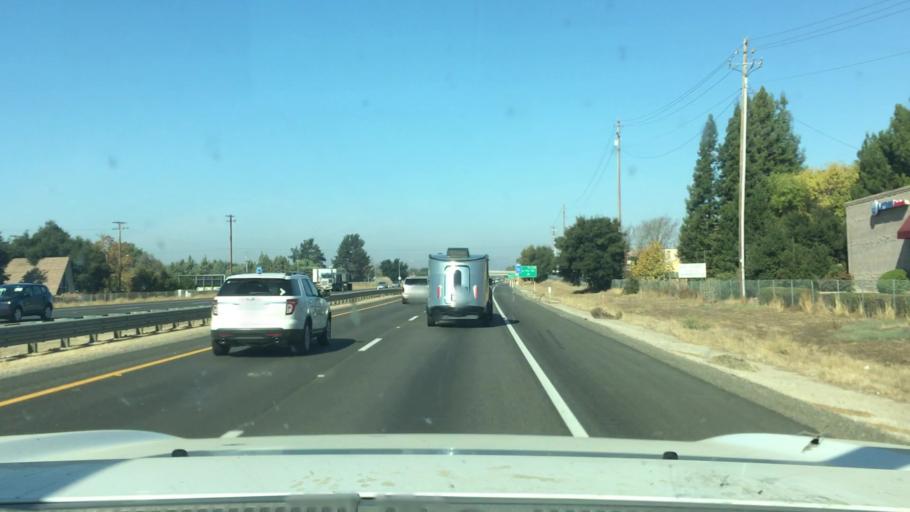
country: US
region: California
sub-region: San Luis Obispo County
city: Atascadero
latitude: 35.5087
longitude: -120.6960
